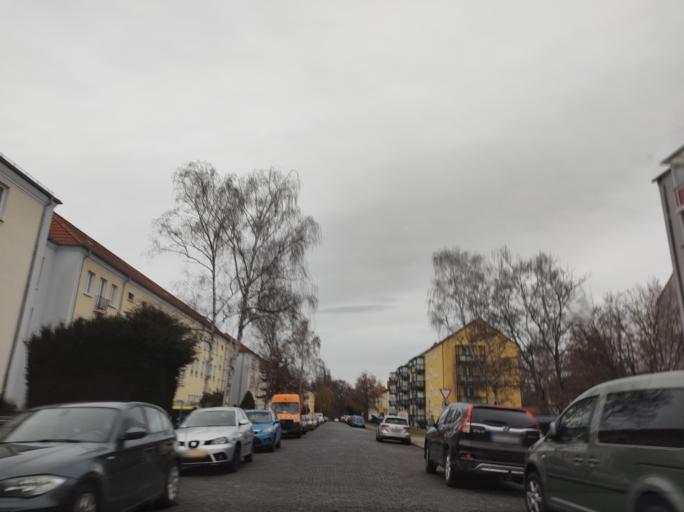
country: DE
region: Saxony-Anhalt
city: Zeitz
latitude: 51.0425
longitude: 12.1279
